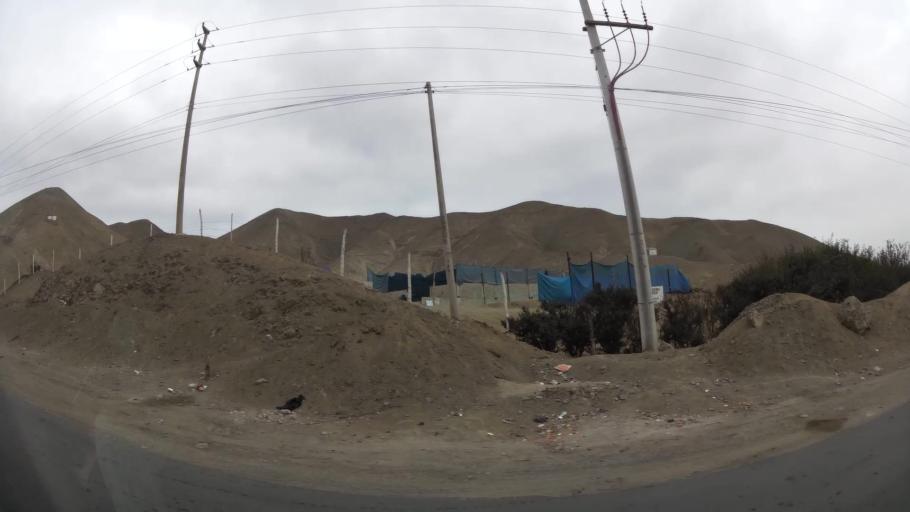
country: PE
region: Lima
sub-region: Lima
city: San Bartolo
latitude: -12.4030
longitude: -76.7567
